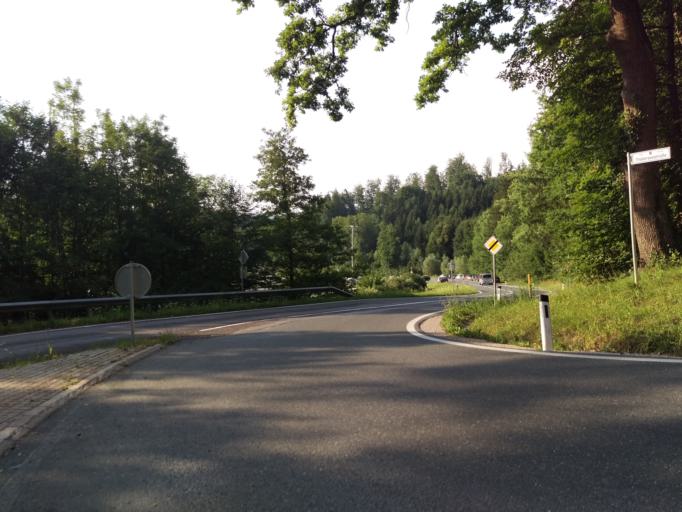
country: AT
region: Styria
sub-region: Politischer Bezirk Graz-Umgebung
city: Thal
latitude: 47.0574
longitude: 15.3669
